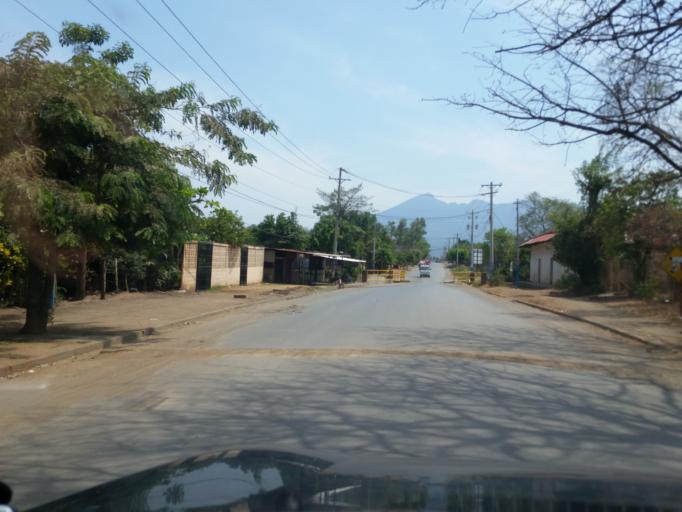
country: NI
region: Granada
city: Granada
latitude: 11.9429
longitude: -85.9621
